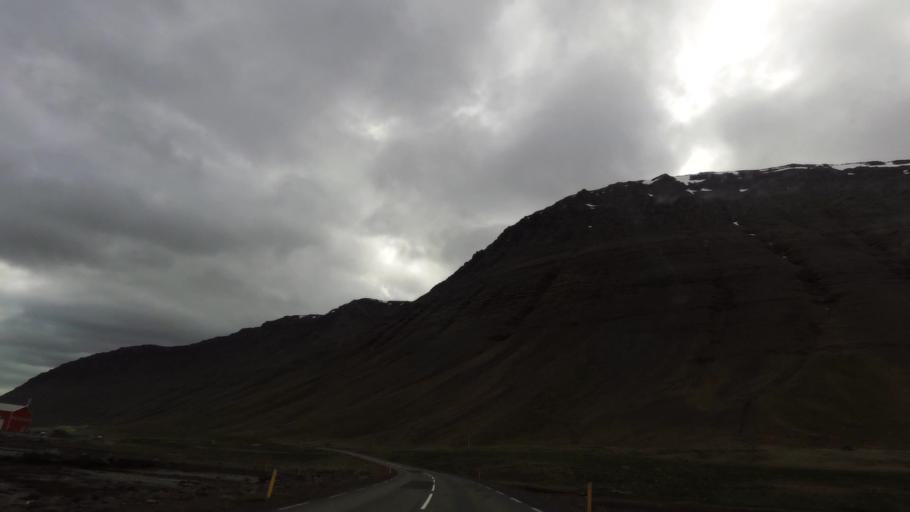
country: IS
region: Westfjords
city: Isafjoerdur
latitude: 66.0528
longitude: -23.1485
